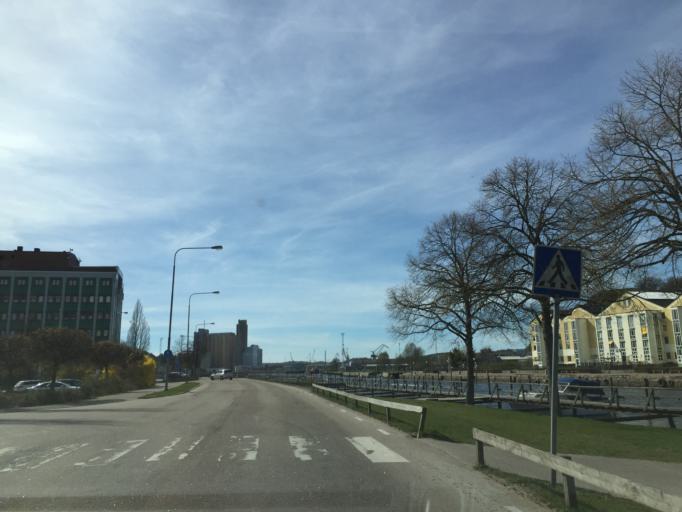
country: SE
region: Vaestra Goetaland
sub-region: Uddevalla Kommun
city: Uddevalla
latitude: 58.3482
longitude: 11.9278
